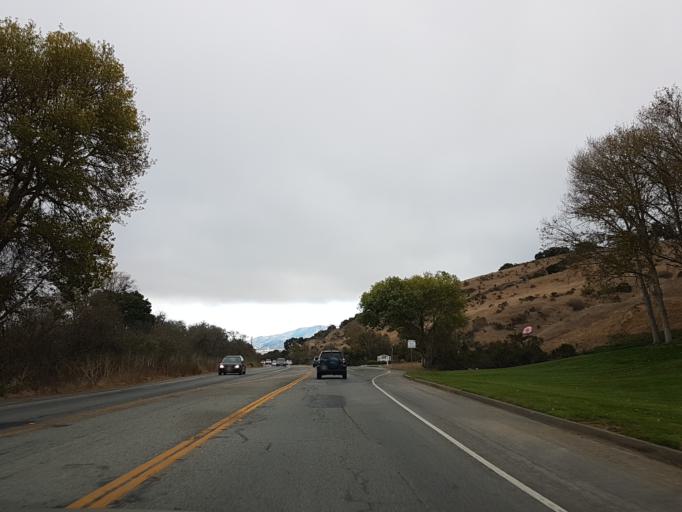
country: US
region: California
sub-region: Monterey County
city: Salinas
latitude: 36.6179
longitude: -121.6606
